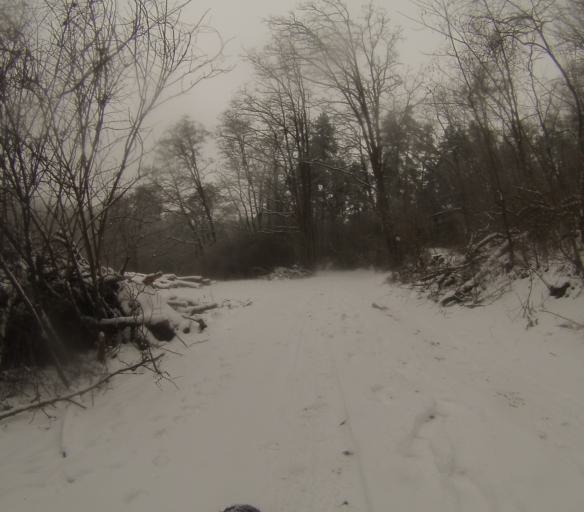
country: CZ
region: South Moravian
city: Zelesice
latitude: 49.1299
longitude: 16.5545
